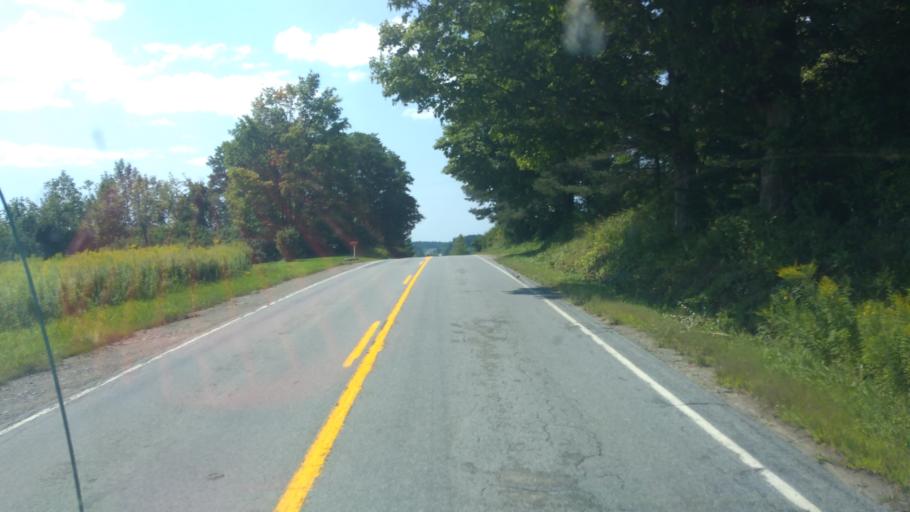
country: US
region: New York
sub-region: Steuben County
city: Canisteo
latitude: 42.3333
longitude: -77.5839
